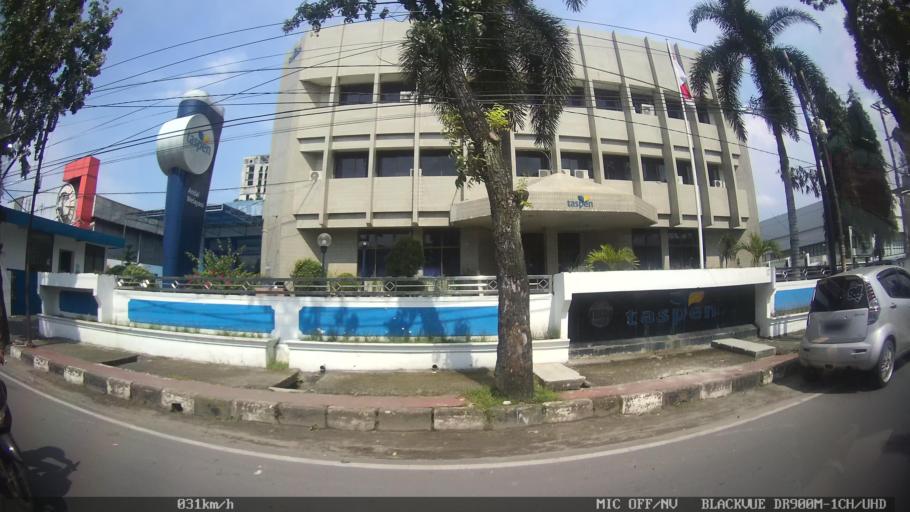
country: ID
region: North Sumatra
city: Medan
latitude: 3.6029
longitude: 98.6691
